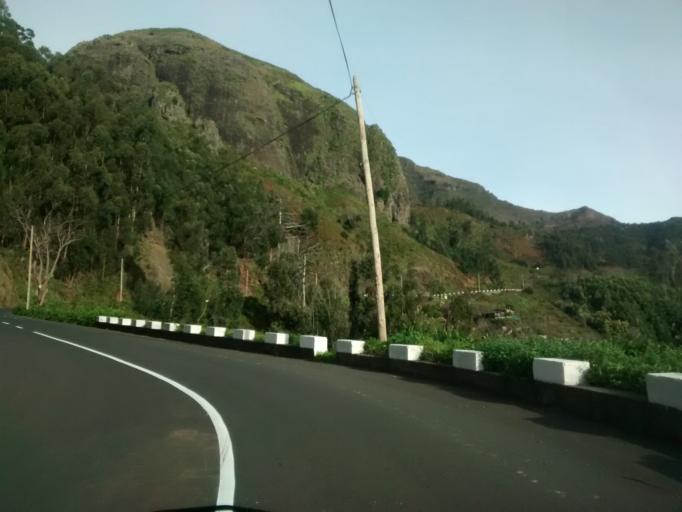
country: PT
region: Madeira
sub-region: Camara de Lobos
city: Curral das Freiras
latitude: 32.7393
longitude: -17.0248
